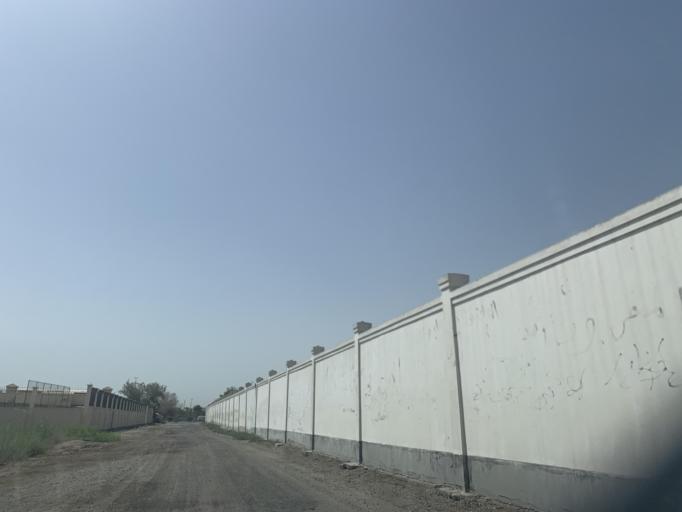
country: BH
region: Manama
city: Jidd Hafs
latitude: 26.2017
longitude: 50.5564
